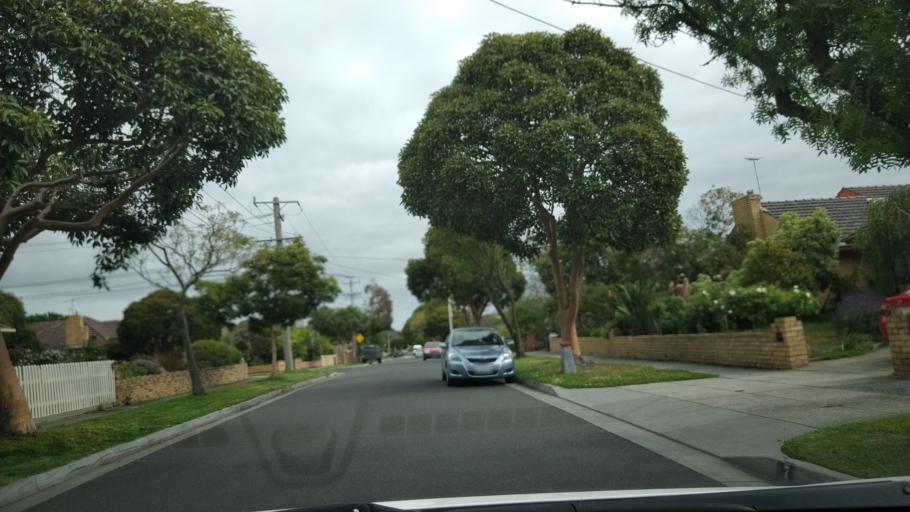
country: AU
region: Victoria
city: Hughesdale
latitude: -37.9069
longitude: 145.0954
